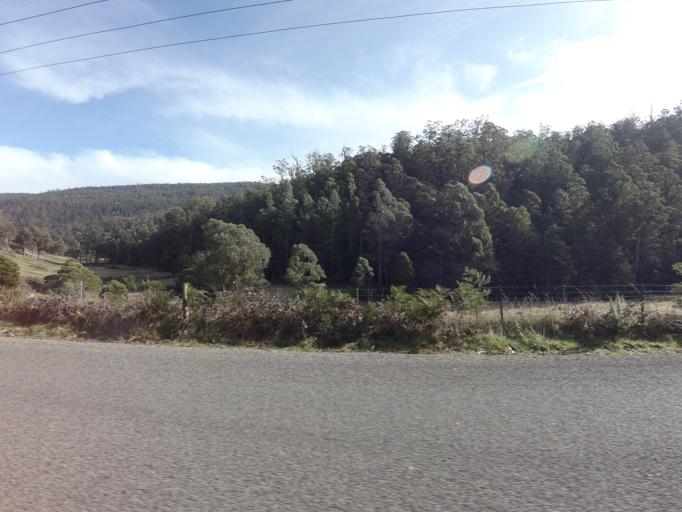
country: AU
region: Tasmania
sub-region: Huon Valley
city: Huonville
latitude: -43.0432
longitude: 147.1248
